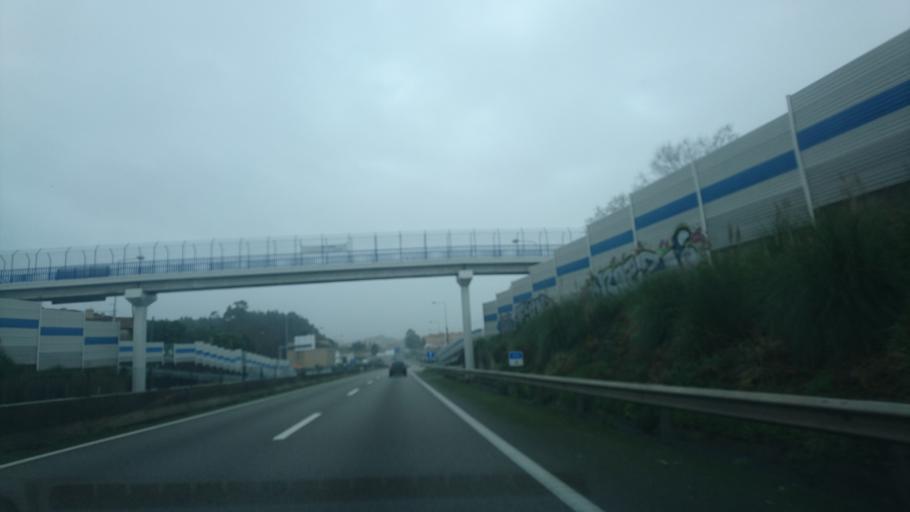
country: PT
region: Porto
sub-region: Vila Nova de Gaia
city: Vilar do Paraiso
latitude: 41.1071
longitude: -8.6265
